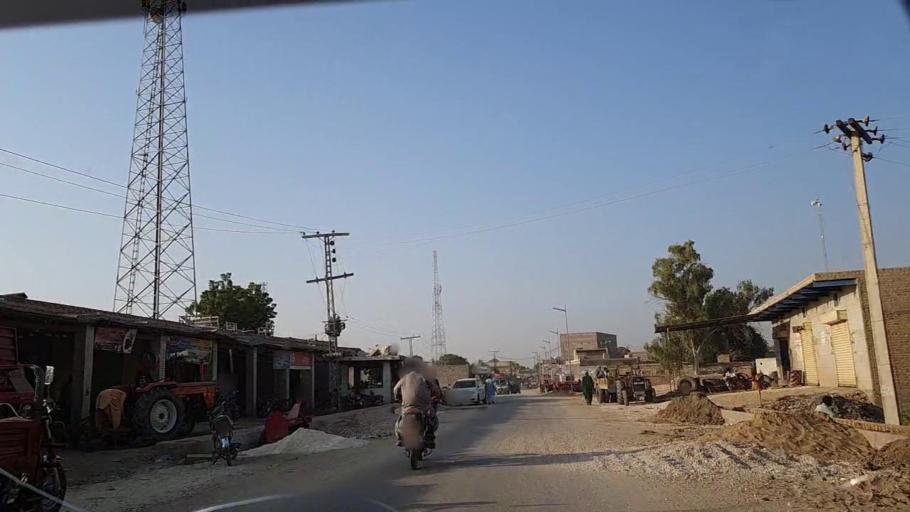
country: PK
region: Sindh
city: Rustam jo Goth
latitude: 27.9630
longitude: 68.8058
